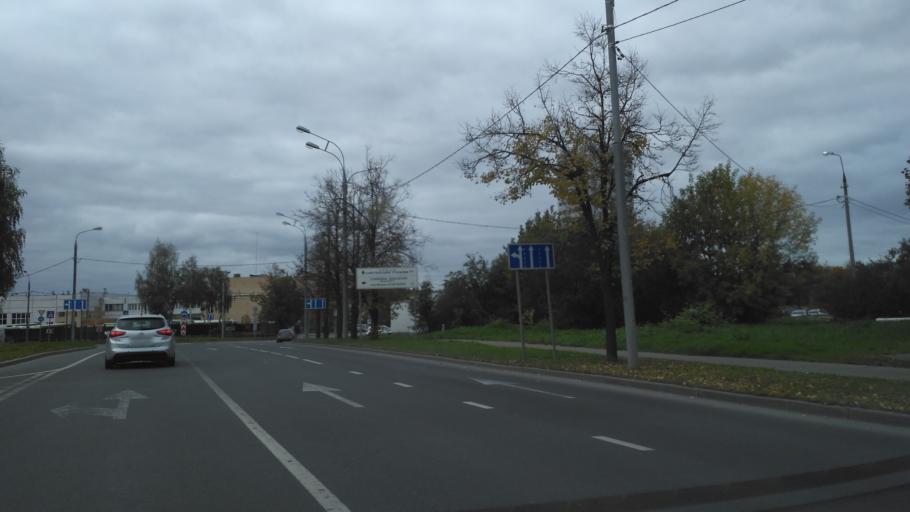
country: RU
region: Moscow
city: Zelenograd
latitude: 56.0098
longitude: 37.1939
